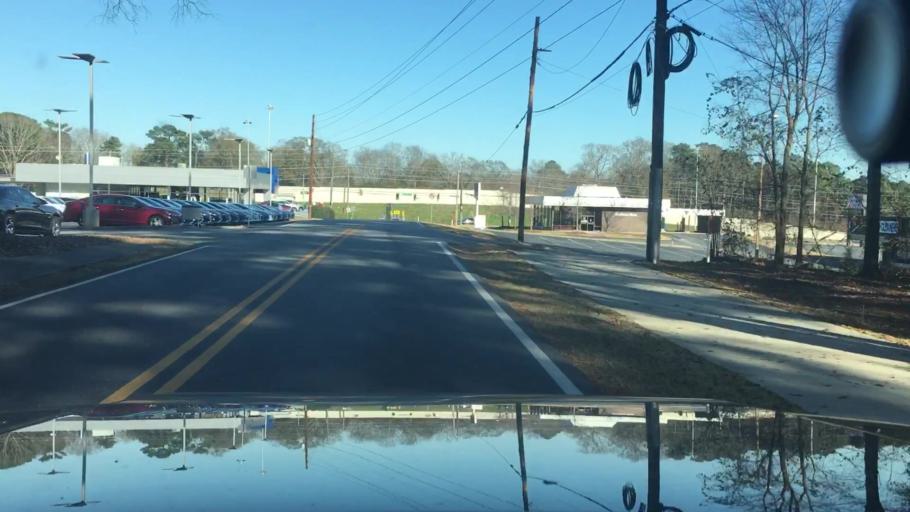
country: US
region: Georgia
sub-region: Bibb County
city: Macon
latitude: 32.8856
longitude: -83.6750
